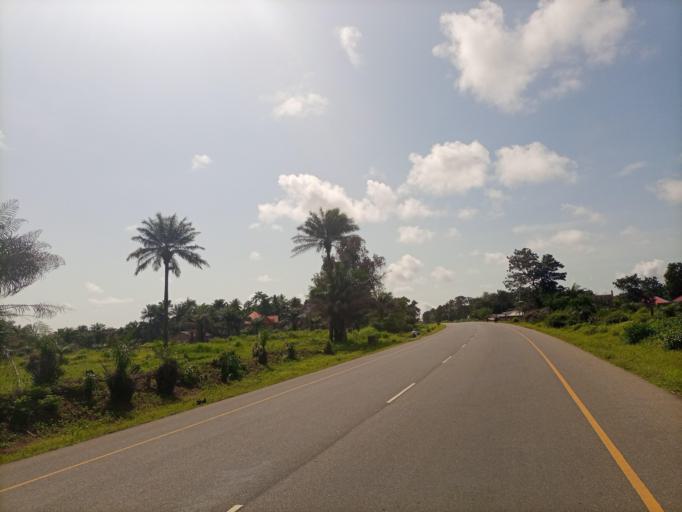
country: SL
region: Northern Province
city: Masoyila
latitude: 8.6230
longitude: -13.1762
